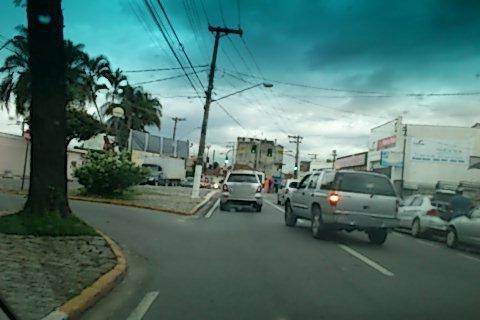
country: BR
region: Sao Paulo
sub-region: Jacarei
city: Jacarei
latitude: -23.2971
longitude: -45.9670
